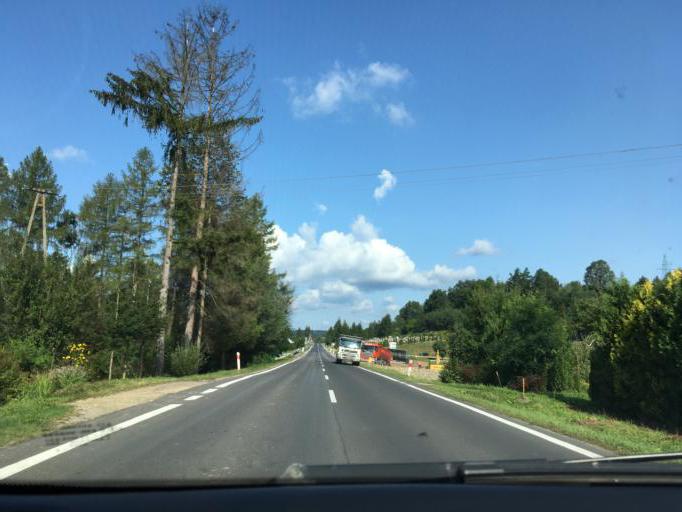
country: PL
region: Subcarpathian Voivodeship
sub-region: Powiat leski
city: Olszanica
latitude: 49.4688
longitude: 22.4619
